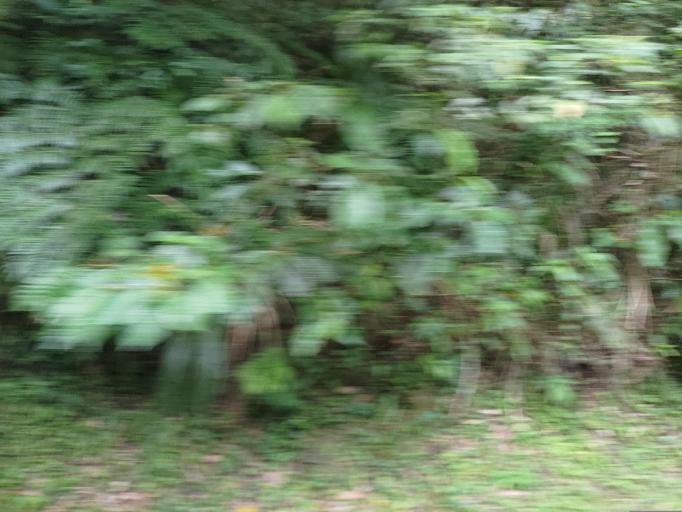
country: TW
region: Taiwan
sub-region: Hsinchu
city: Hsinchu
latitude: 24.6079
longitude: 121.0401
